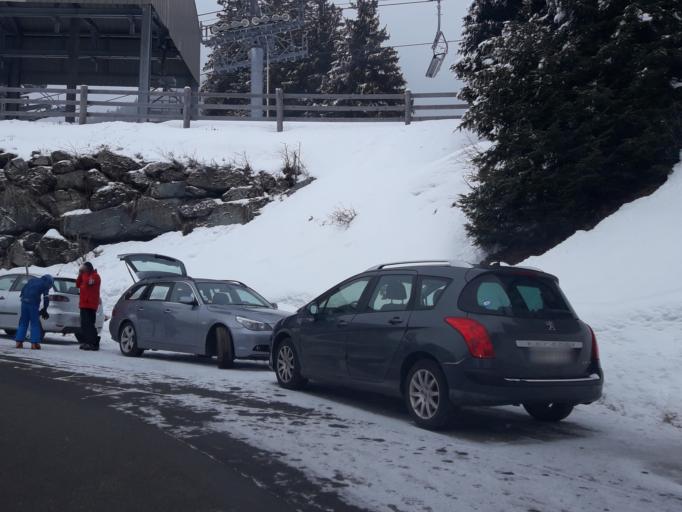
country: FR
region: Rhone-Alpes
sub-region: Departement de l'Isere
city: Theys
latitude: 45.2639
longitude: 6.0159
